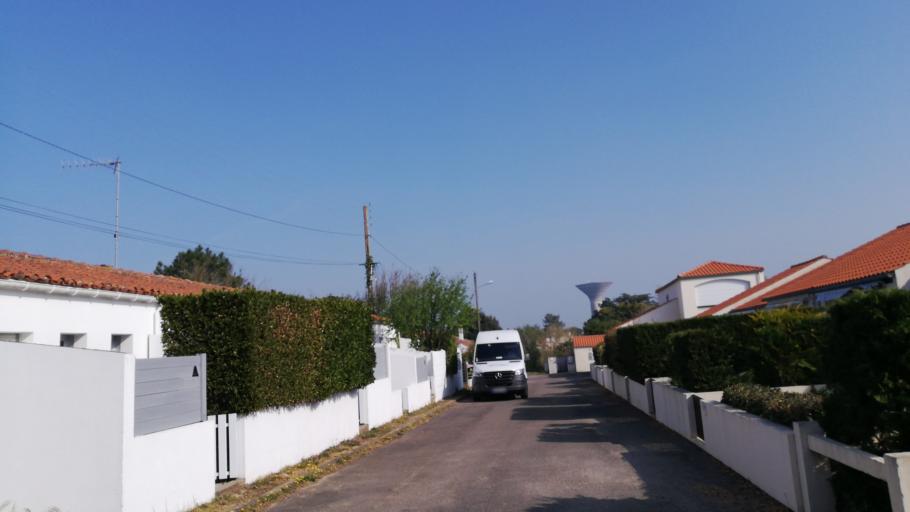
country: FR
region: Pays de la Loire
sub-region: Departement de la Vendee
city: La Tranche-sur-Mer
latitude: 46.3495
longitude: -1.4186
